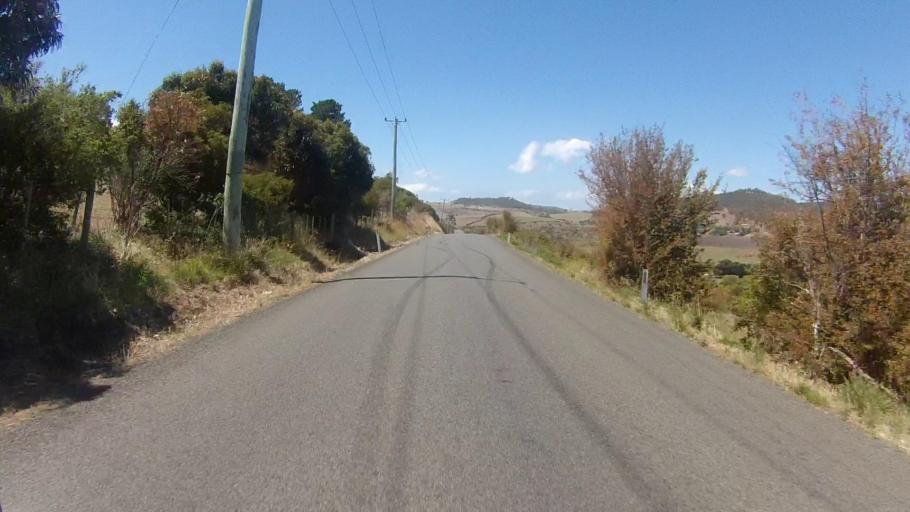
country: AU
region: Tasmania
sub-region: Sorell
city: Sorell
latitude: -42.7729
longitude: 147.5850
